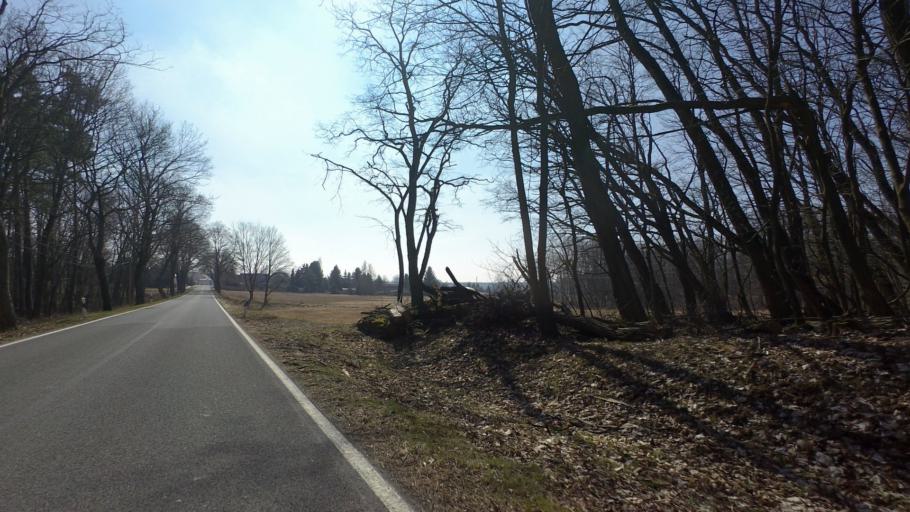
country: DE
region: Saxony-Anhalt
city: Nudersdorf
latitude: 52.0241
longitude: 12.5304
